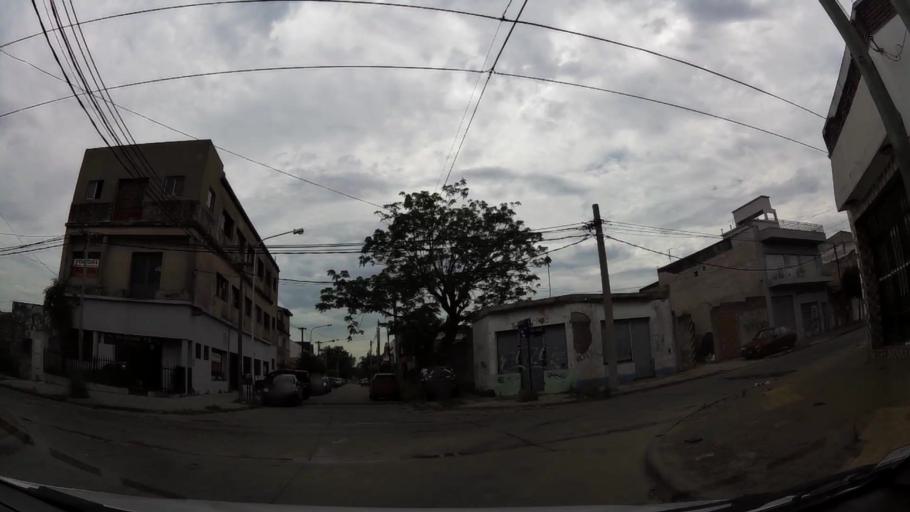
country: AR
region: Buenos Aires F.D.
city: Villa Lugano
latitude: -34.6786
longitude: -58.5033
